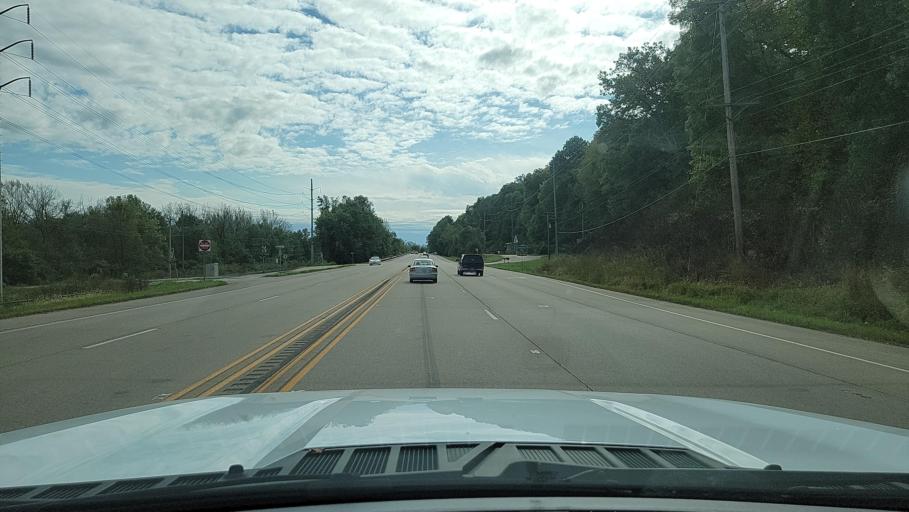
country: US
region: Illinois
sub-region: Peoria County
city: Bartonville
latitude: 40.6185
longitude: -89.6572
